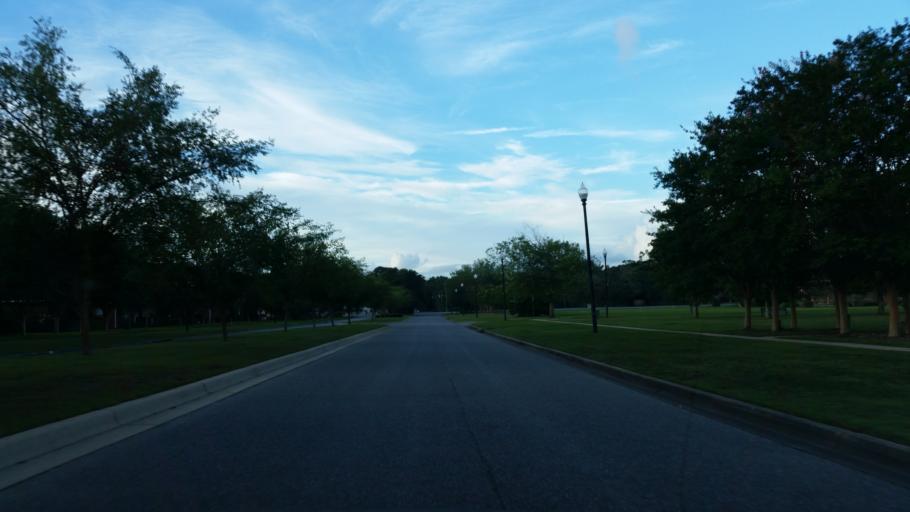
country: US
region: Florida
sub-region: Escambia County
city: Ensley
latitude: 30.5363
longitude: -87.3079
